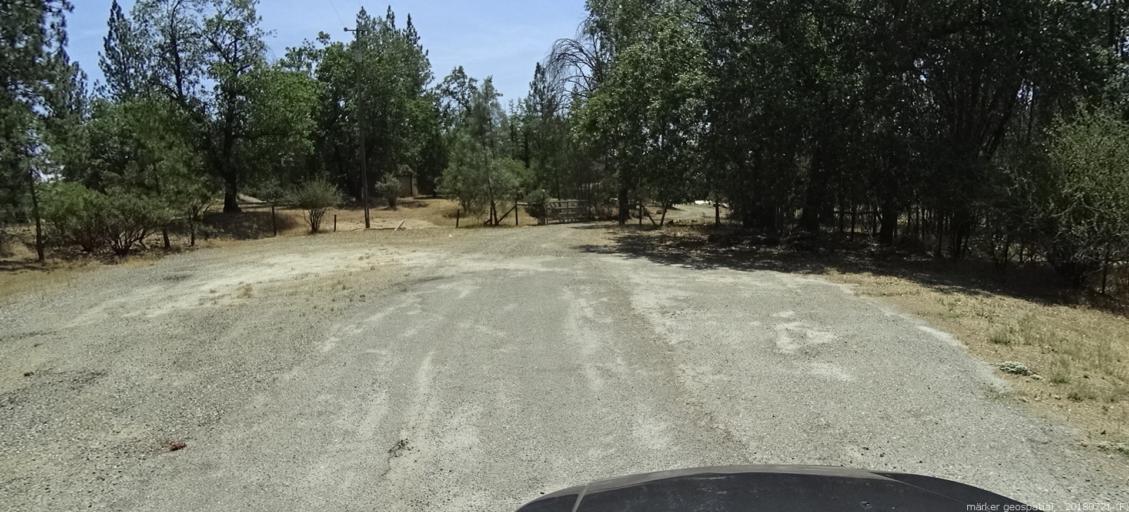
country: US
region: California
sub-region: Madera County
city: Oakhurst
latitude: 37.2325
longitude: -119.5437
